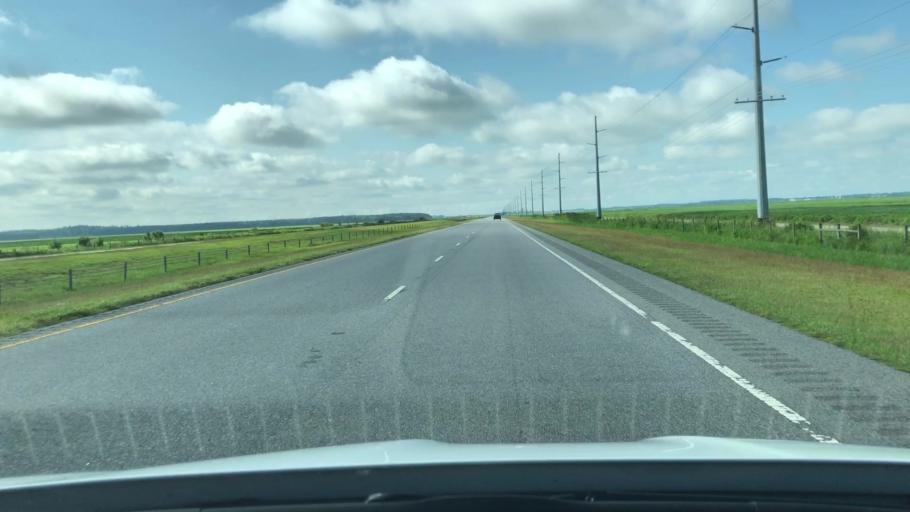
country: US
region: North Carolina
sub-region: Pasquotank County
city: Elizabeth City
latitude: 36.3257
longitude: -76.3106
